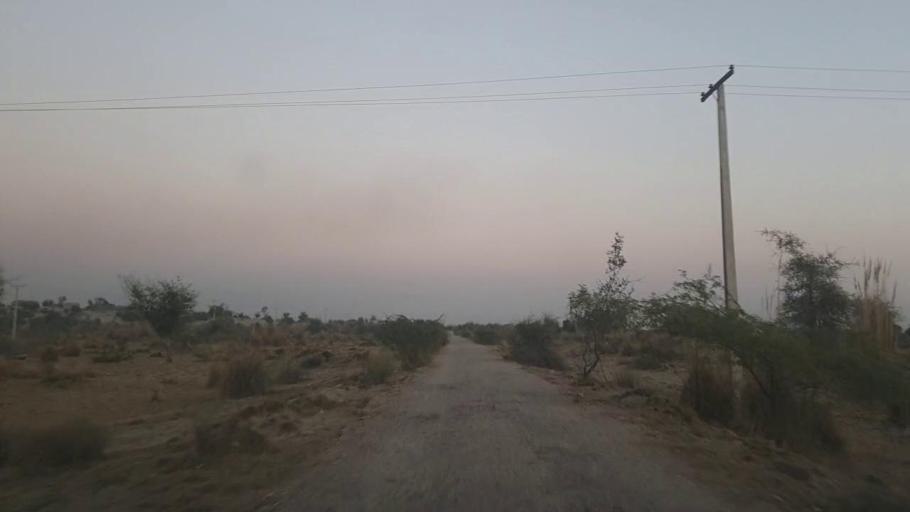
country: PK
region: Sindh
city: Jam Sahib
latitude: 26.3868
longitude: 68.8119
